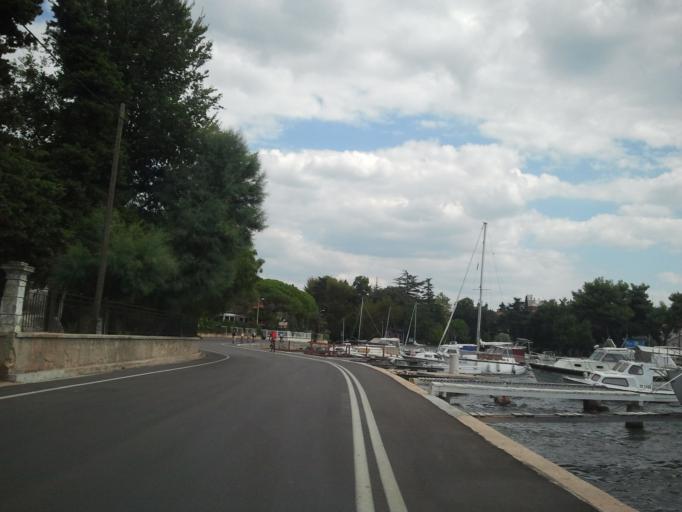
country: HR
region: Zadarska
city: Zadar
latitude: 44.1257
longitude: 15.2235
